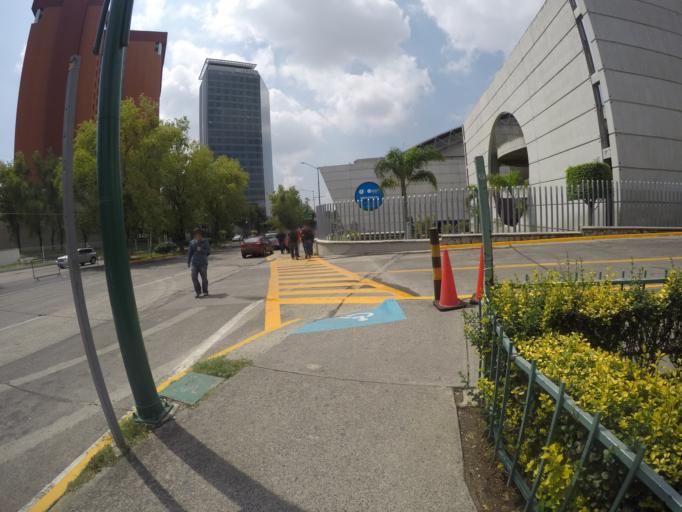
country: MX
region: Jalisco
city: Guadalajara
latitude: 20.6536
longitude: -103.3903
